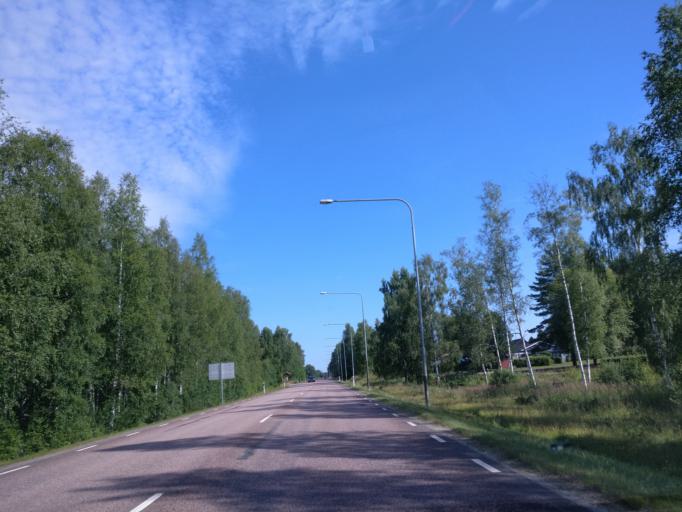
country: SE
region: Vaermland
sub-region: Hagfors Kommun
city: Hagfors
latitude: 60.0466
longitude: 13.7039
